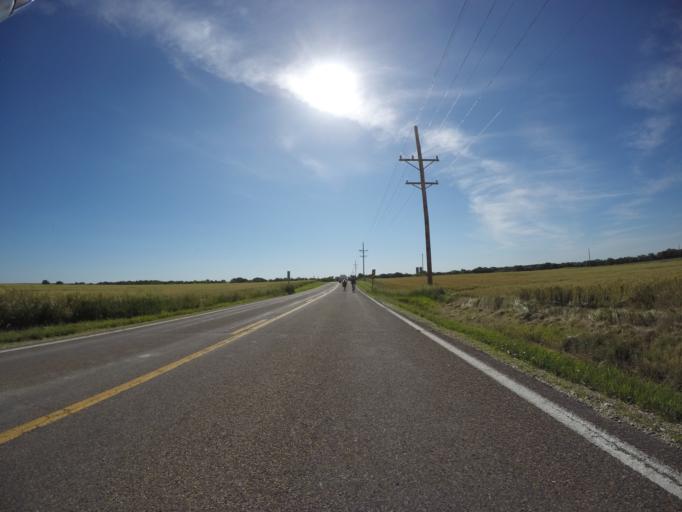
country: US
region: Kansas
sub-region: Mitchell County
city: Beloit
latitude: 39.6393
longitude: -97.9517
